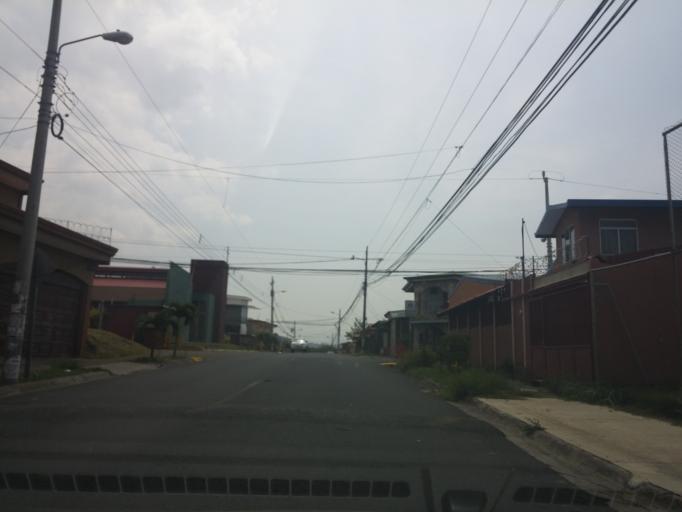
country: CR
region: Heredia
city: San Francisco
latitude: 9.9865
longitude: -84.1324
